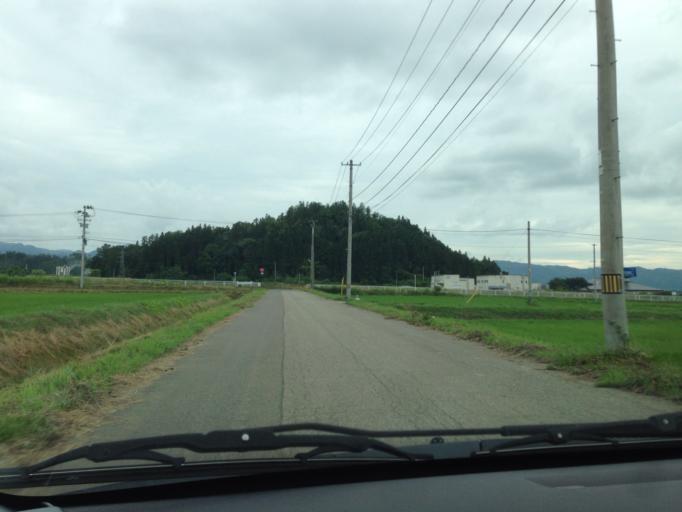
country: JP
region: Fukushima
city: Kitakata
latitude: 37.4343
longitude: 139.8831
